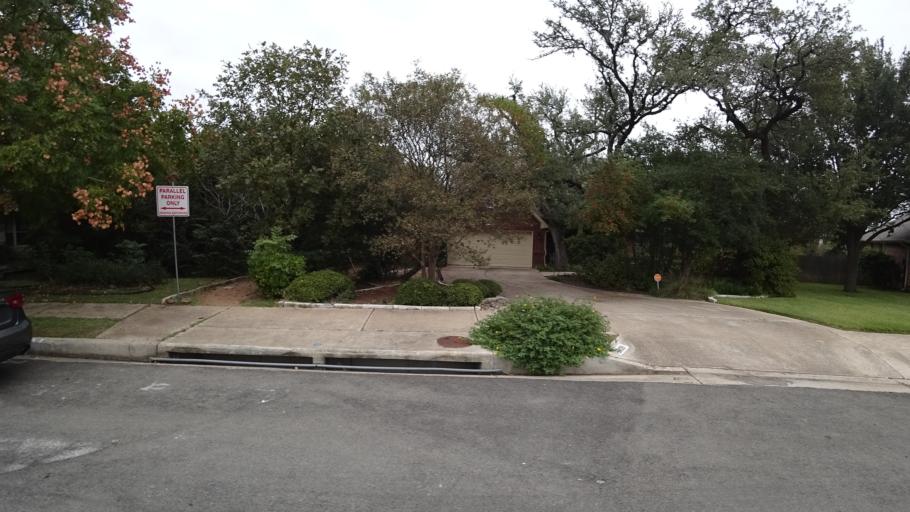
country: US
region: Texas
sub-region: Travis County
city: Shady Hollow
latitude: 30.2095
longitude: -97.8786
